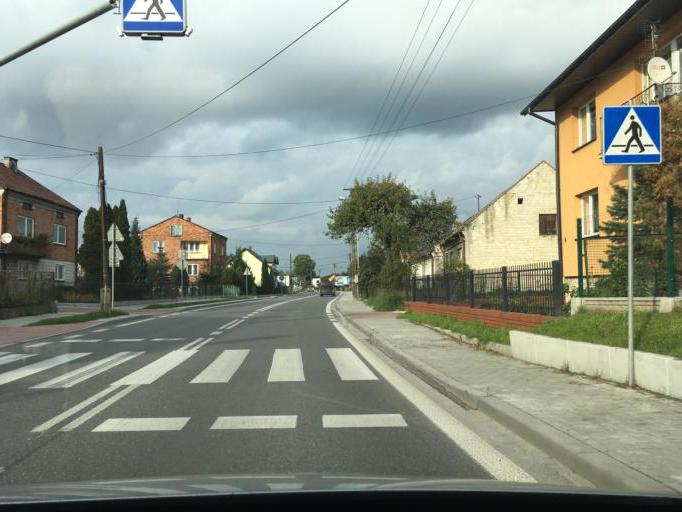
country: PL
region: Swietokrzyskie
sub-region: Powiat pinczowski
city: Pinczow
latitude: 50.5249
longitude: 20.5338
